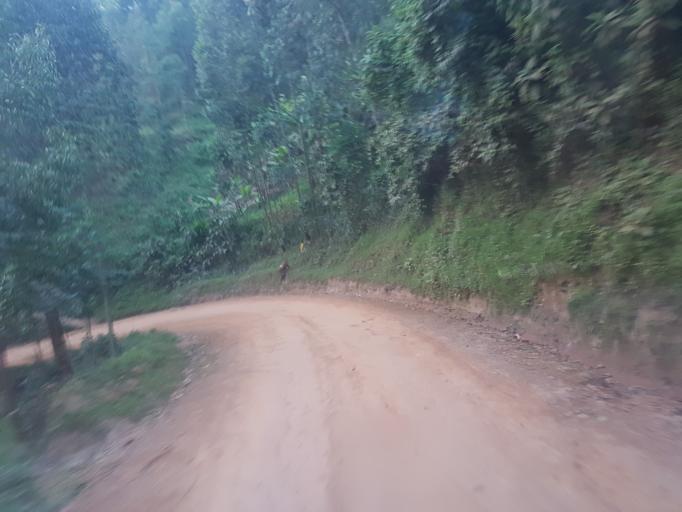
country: UG
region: Western Region
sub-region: Kanungu District
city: Kanungu
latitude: -0.9499
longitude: 29.8266
